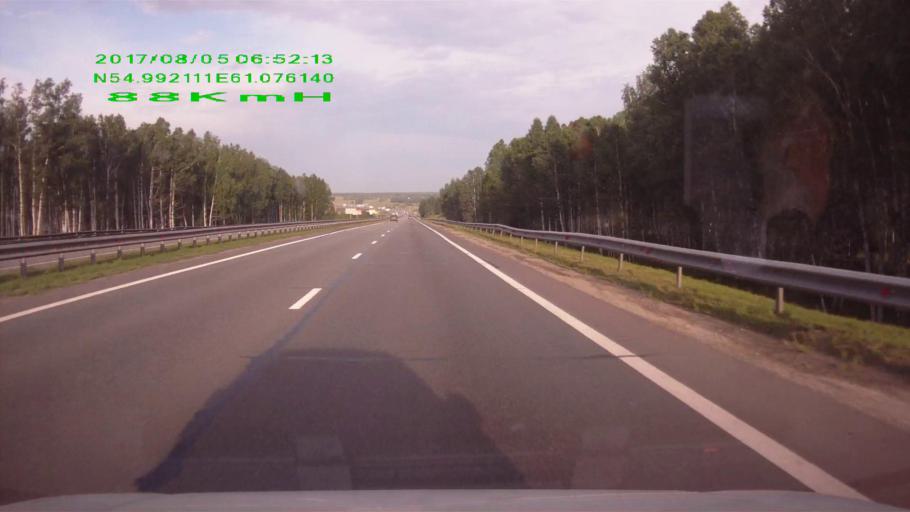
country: RU
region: Chelyabinsk
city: Poletayevo
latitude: 54.9921
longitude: 61.0758
